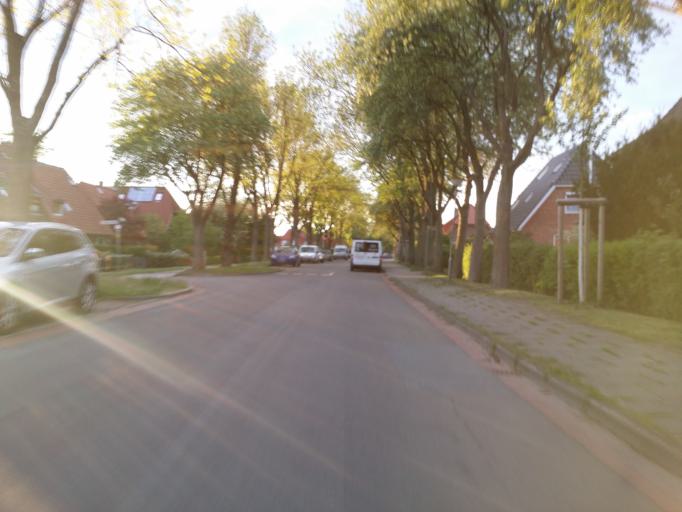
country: DE
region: Lower Saxony
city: Stuhr
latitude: 53.0545
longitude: 8.7657
